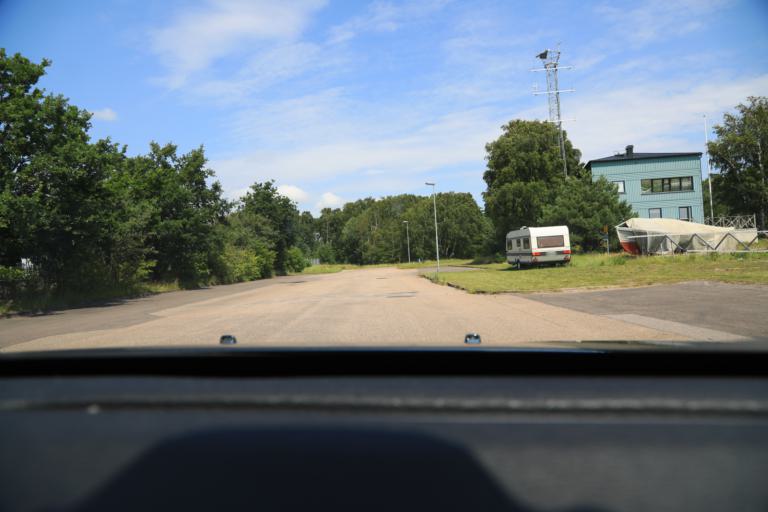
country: SE
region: Halland
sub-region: Halmstads Kommun
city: Halmstad
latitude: 56.6611
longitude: 12.8507
